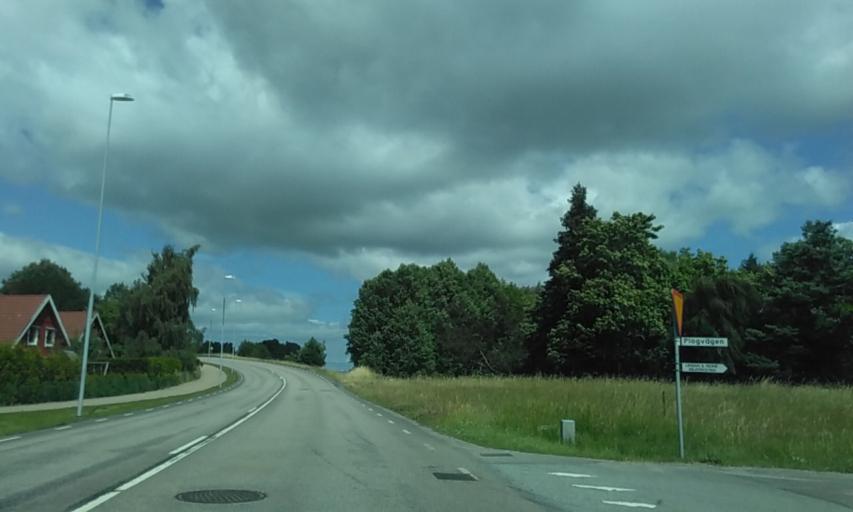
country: SE
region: Vaestra Goetaland
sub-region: Grastorps Kommun
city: Graestorp
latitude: 58.3321
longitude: 12.6914
